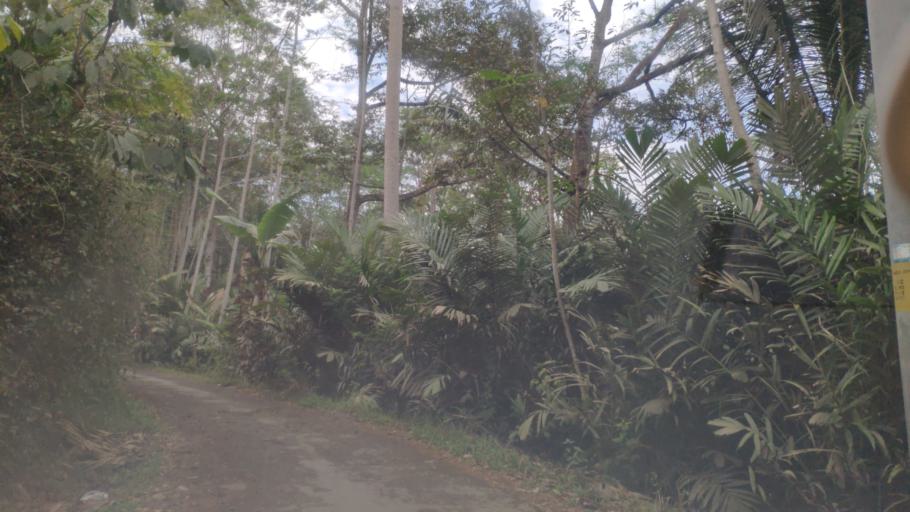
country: ID
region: Central Java
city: Wonosobo
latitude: -7.4452
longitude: 109.8270
